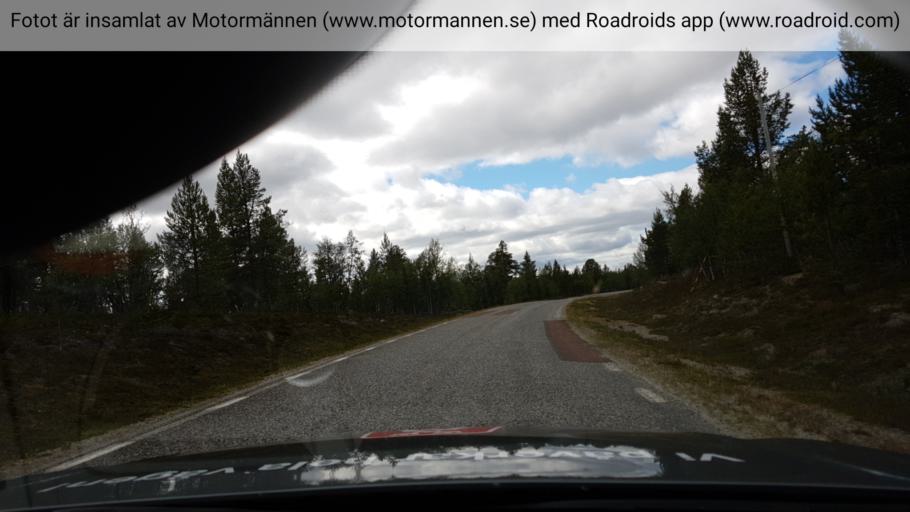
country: NO
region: Hedmark
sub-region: Engerdal
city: Engerdal
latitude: 62.2794
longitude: 12.8641
